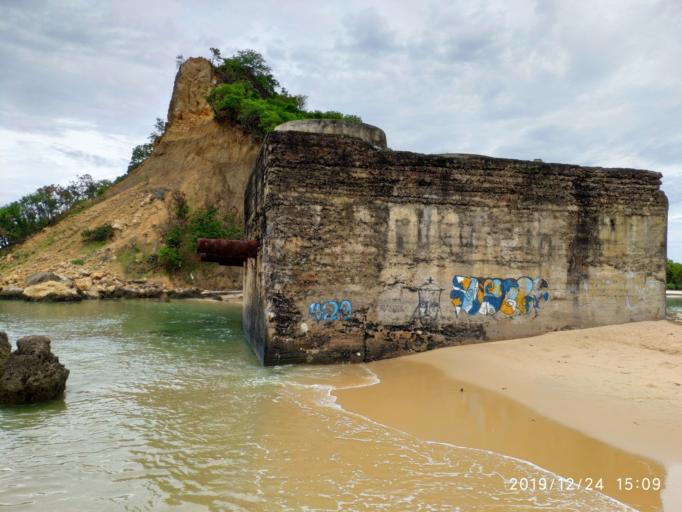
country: MG
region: Diana
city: Antsiranana
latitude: -12.2643
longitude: 49.2992
